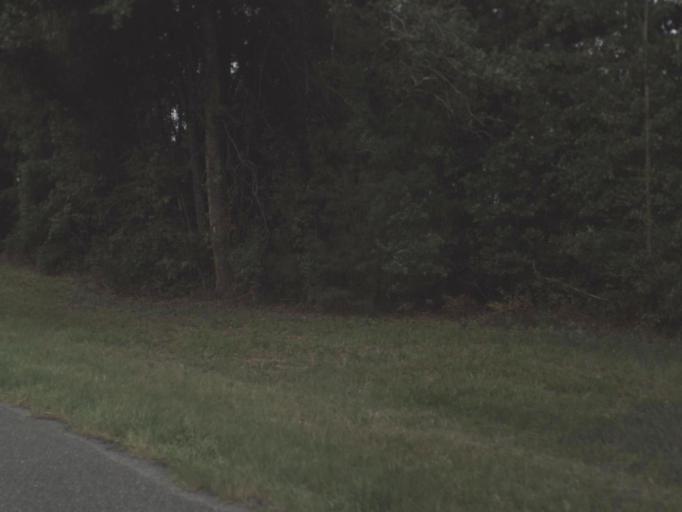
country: US
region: Florida
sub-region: Alachua County
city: Newberry
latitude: 29.6226
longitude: -82.5991
